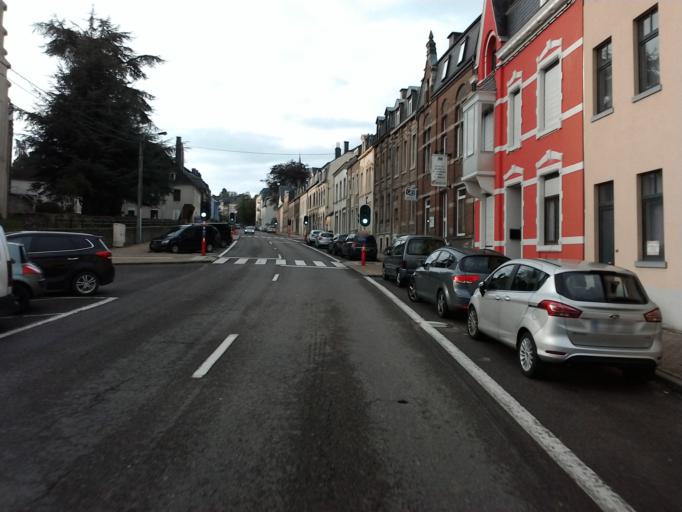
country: BE
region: Wallonia
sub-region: Province du Luxembourg
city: Arlon
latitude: 49.6883
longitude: 5.8102
